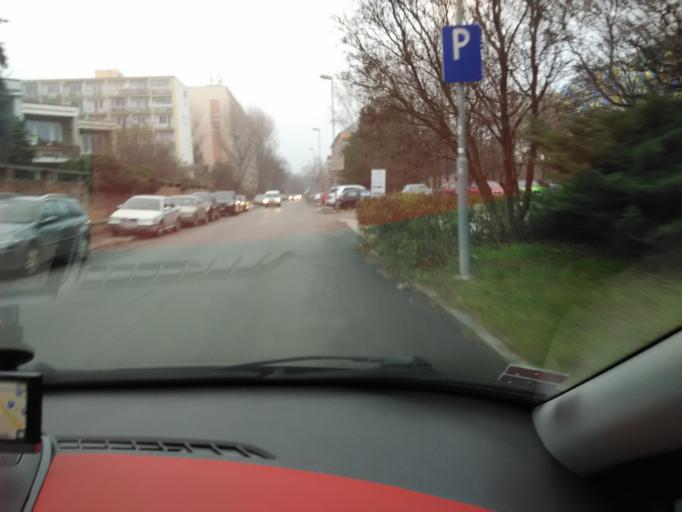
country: SK
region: Bratislavsky
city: Bratislava
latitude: 48.1533
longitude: 17.1622
